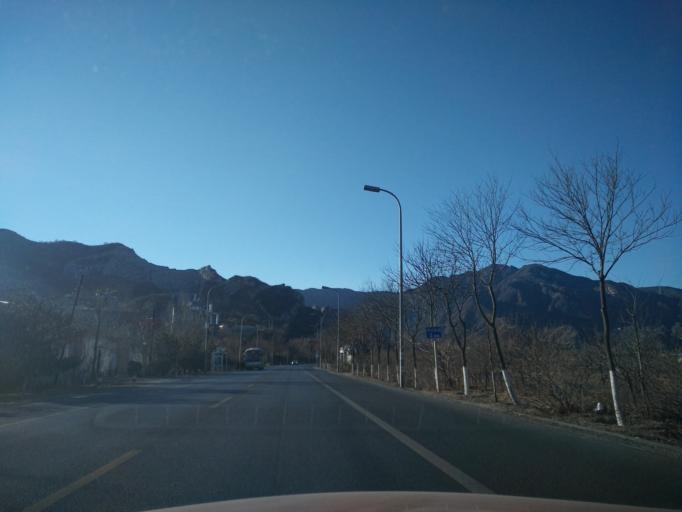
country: CN
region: Beijing
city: Miaofengshan
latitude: 39.9847
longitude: 116.0608
